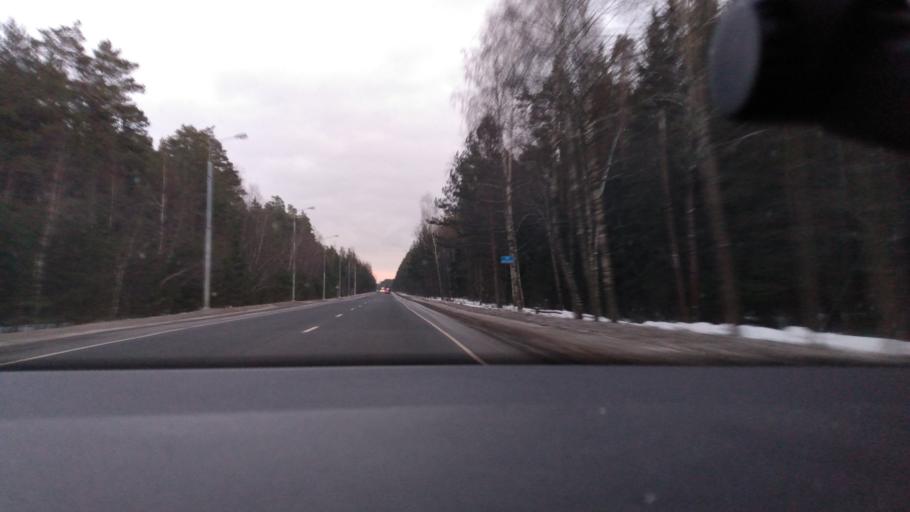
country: RU
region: Moskovskaya
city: Il'inskiy Pogost
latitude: 55.4834
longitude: 38.9276
